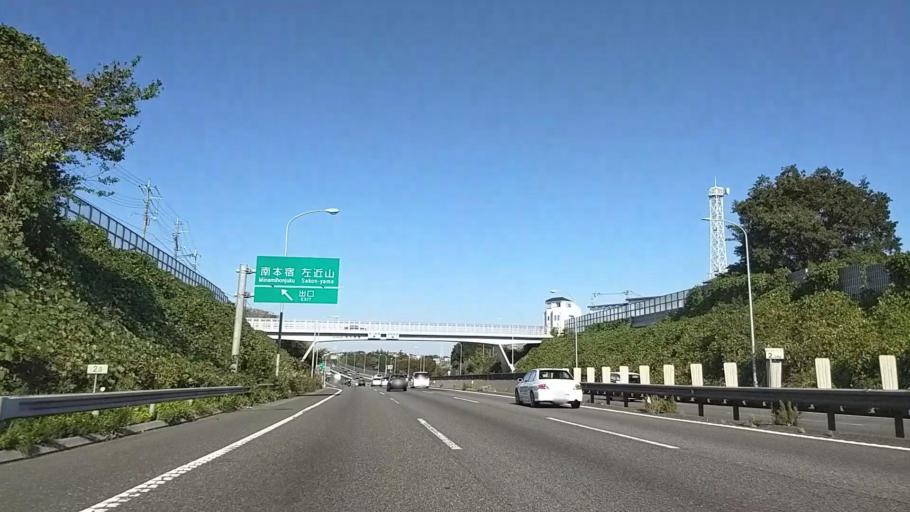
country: JP
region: Kanagawa
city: Yokohama
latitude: 35.4597
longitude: 139.5452
